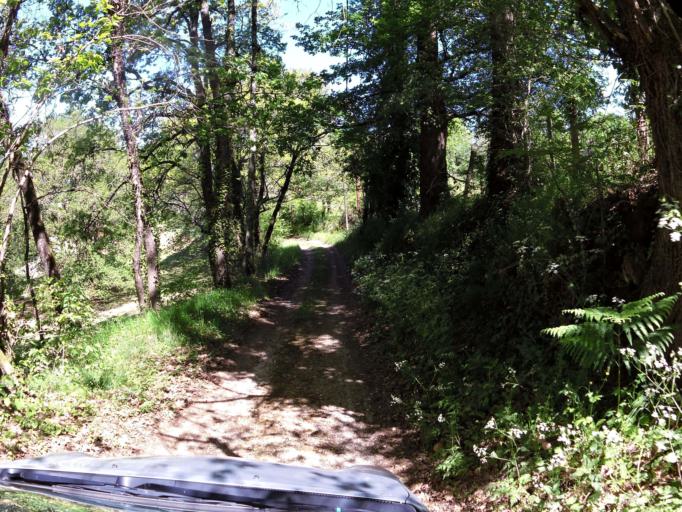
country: FR
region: Aquitaine
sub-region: Departement de la Dordogne
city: Domme
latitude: 44.7906
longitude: 1.2189
